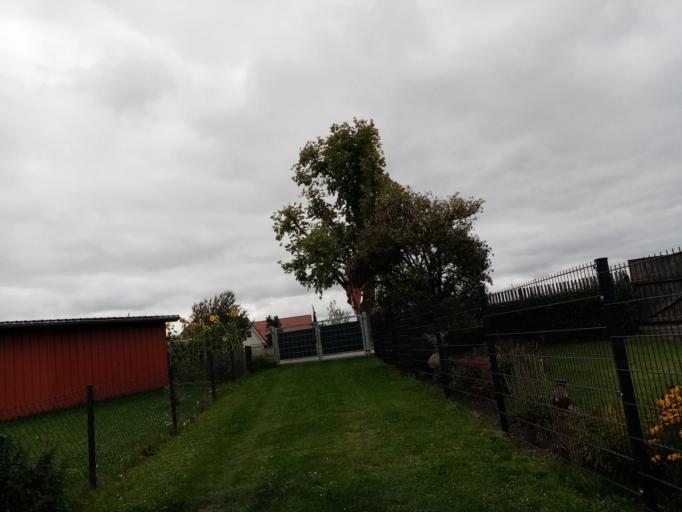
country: DE
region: Thuringia
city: Dingelstadt
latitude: 51.3222
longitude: 10.3115
